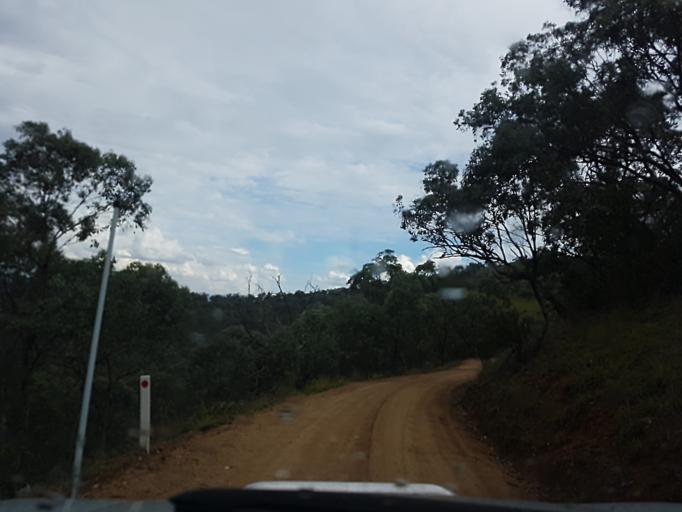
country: AU
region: New South Wales
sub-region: Snowy River
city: Jindabyne
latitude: -36.9445
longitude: 148.3477
